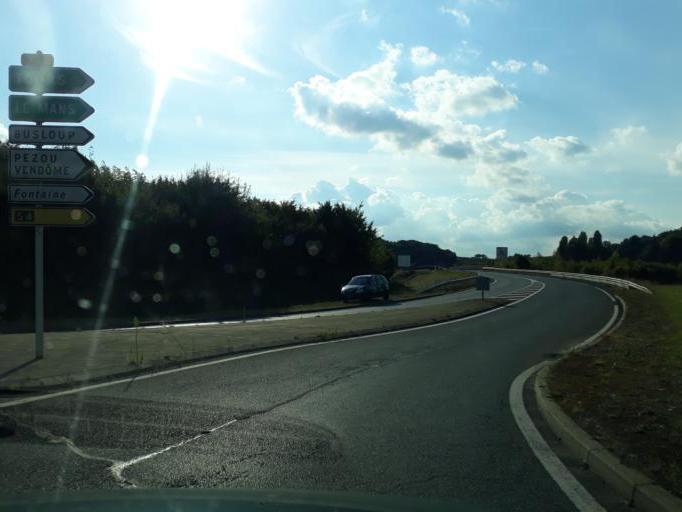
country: FR
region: Centre
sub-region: Departement du Loir-et-Cher
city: Moree
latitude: 47.8915
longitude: 1.1834
